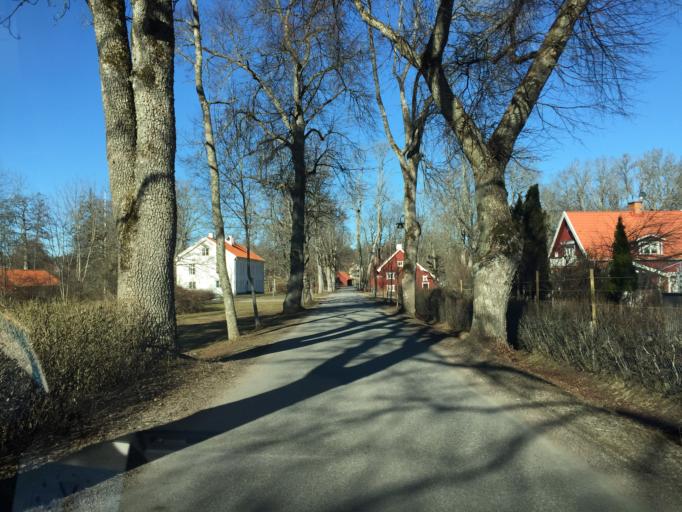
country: SE
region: Soedermanland
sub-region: Vingakers Kommun
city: Vingaker
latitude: 59.0219
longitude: 15.6763
